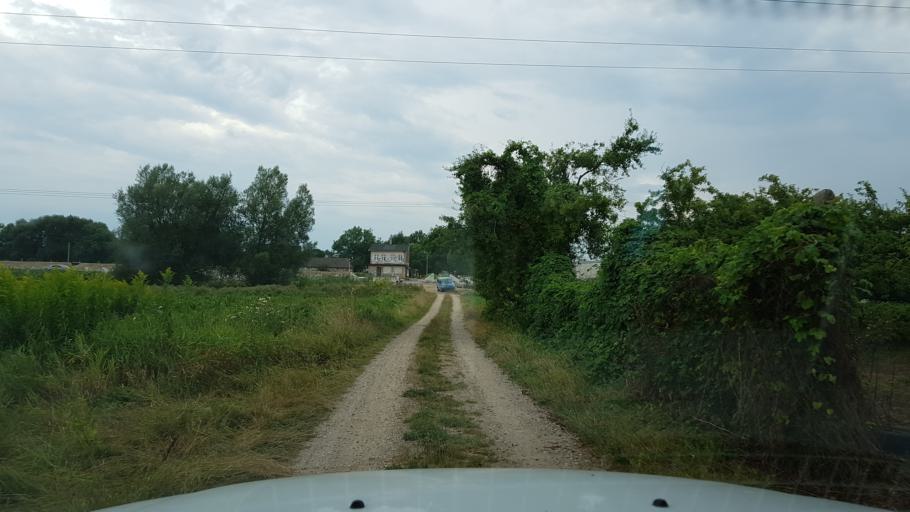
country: PL
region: West Pomeranian Voivodeship
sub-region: Powiat szczecinecki
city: Szczecinek
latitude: 53.7196
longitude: 16.6990
